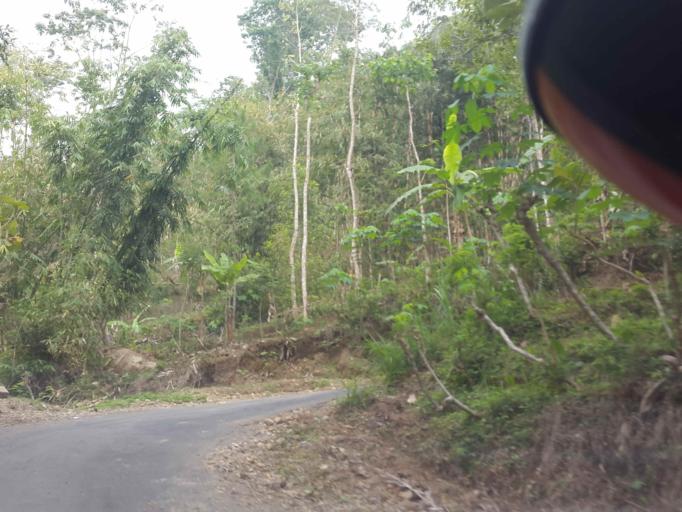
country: ID
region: East Java
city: Ploso
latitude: -8.0401
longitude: 111.1336
